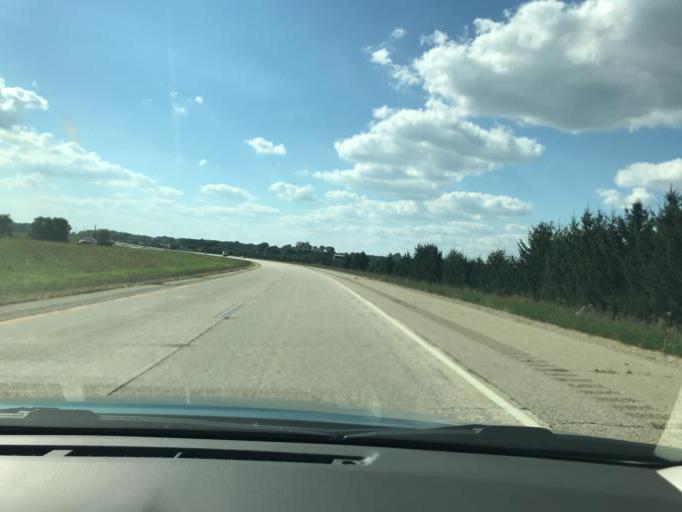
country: US
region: Wisconsin
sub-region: Walworth County
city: Delavan
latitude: 42.6211
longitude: -88.6703
